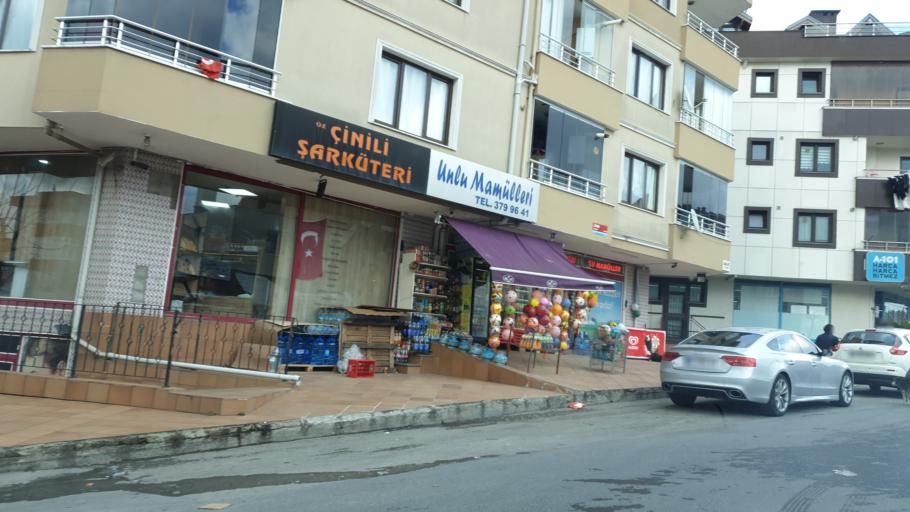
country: TR
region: Istanbul
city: Pendik
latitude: 40.9048
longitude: 29.2469
